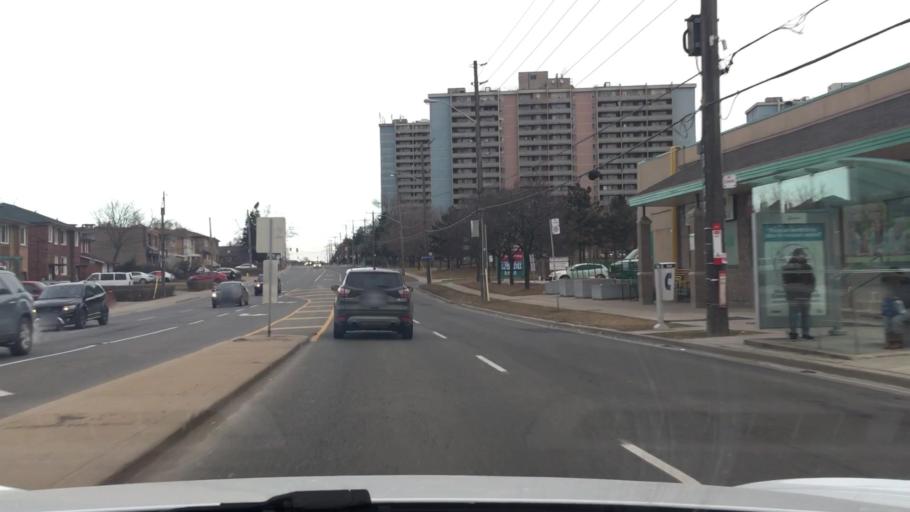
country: CA
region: Ontario
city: Scarborough
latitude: 43.7251
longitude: -79.2538
